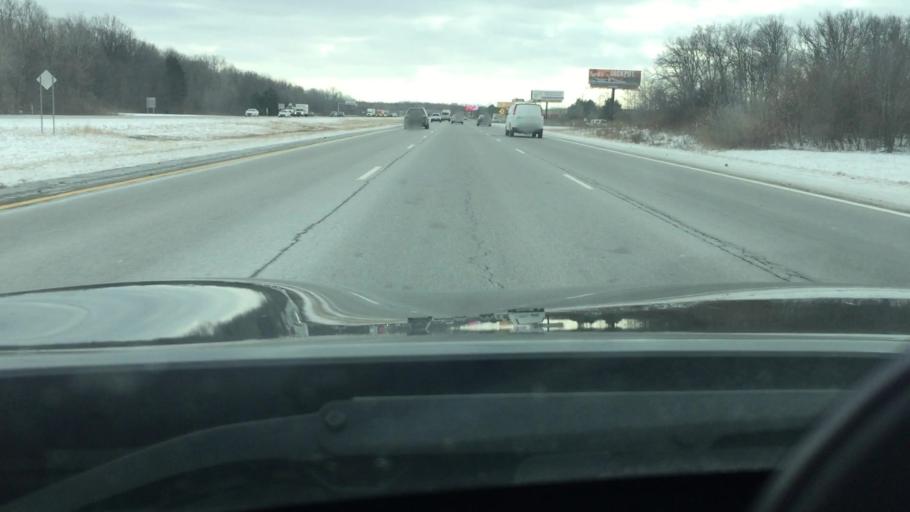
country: US
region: Michigan
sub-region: Wayne County
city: Romulus
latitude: 42.2478
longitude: -83.4402
